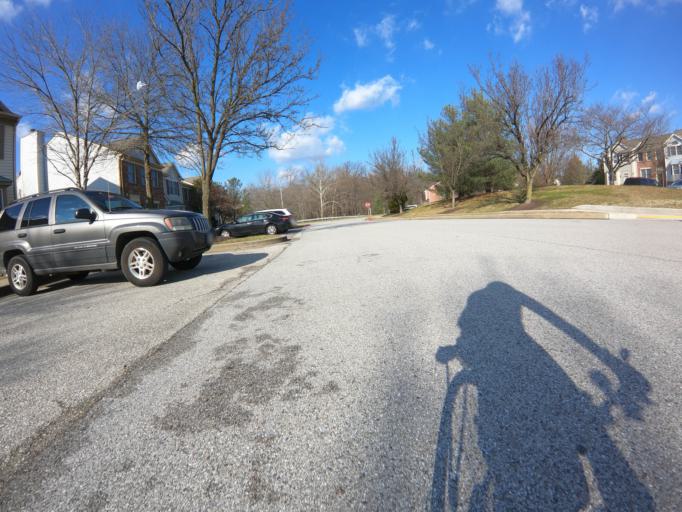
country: US
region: Maryland
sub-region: Howard County
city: Ilchester
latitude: 39.2110
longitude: -76.7878
